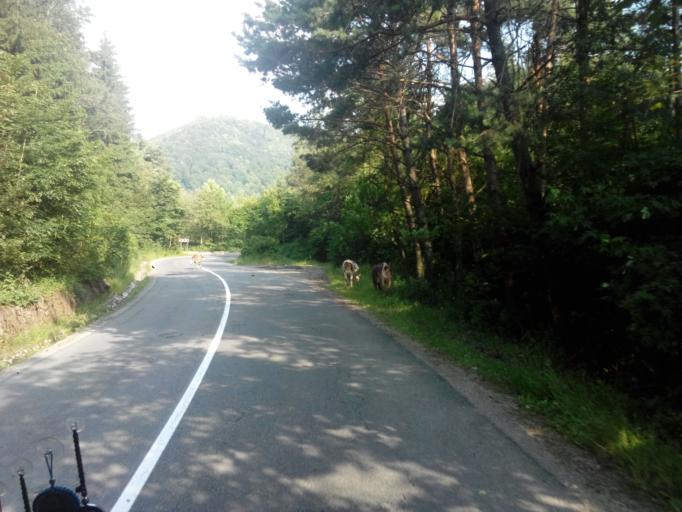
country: RO
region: Brasov
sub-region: Oras Predeal
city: Predeal
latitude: 45.5209
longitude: 25.5056
